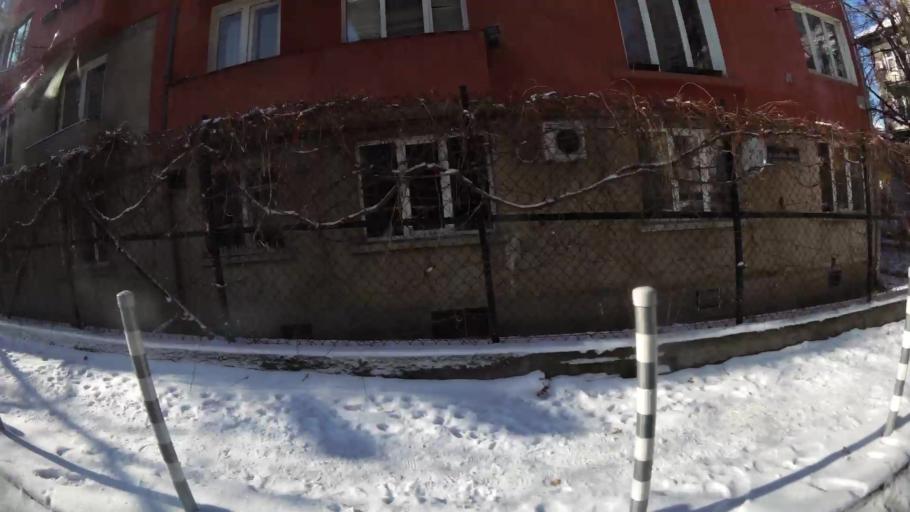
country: BG
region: Sofia-Capital
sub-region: Stolichna Obshtina
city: Sofia
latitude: 42.6806
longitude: 23.3299
